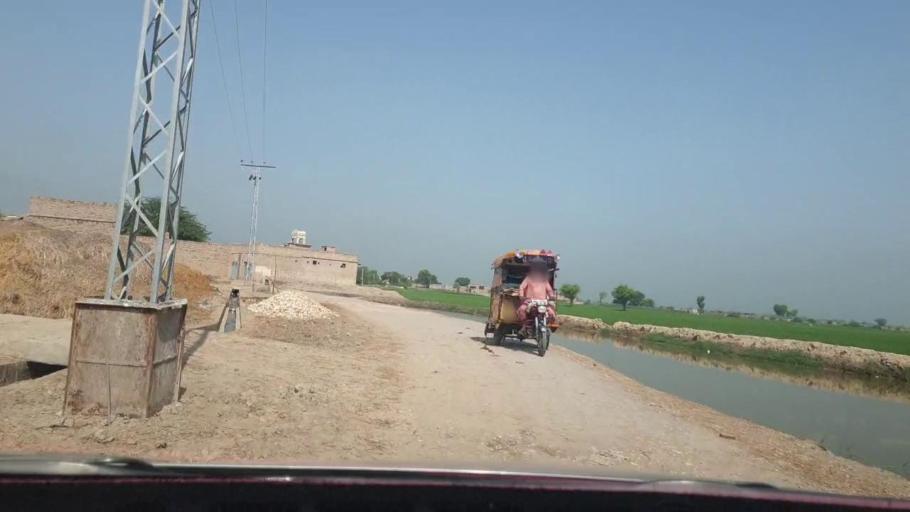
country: PK
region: Sindh
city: Nasirabad
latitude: 27.4239
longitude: 67.9095
